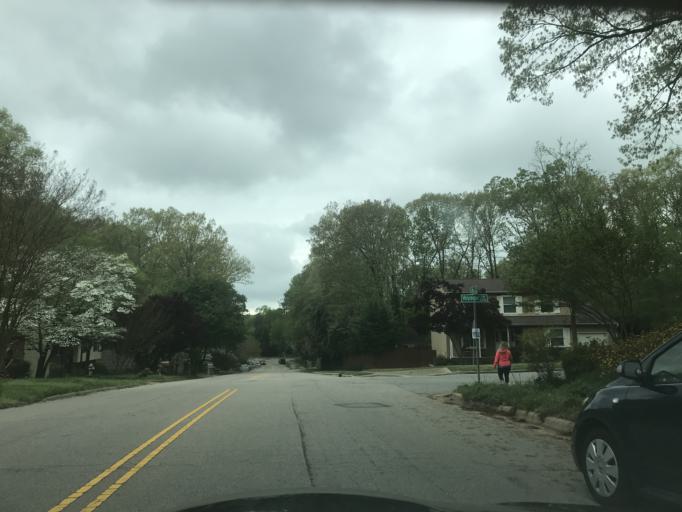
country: US
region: North Carolina
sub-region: Wake County
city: West Raleigh
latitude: 35.7518
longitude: -78.6767
